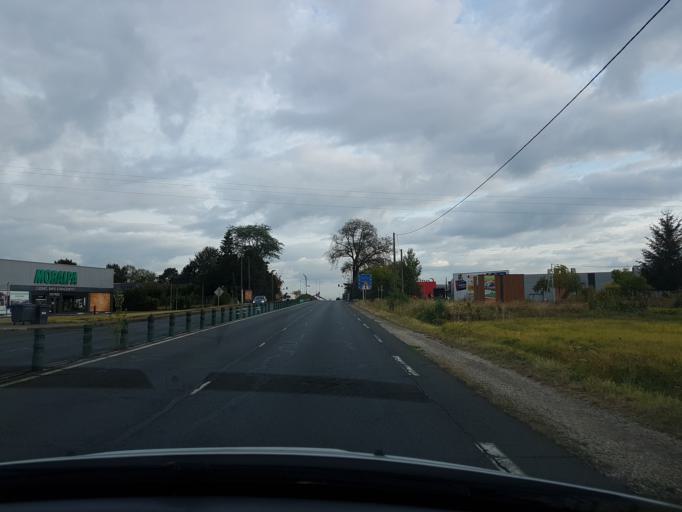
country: FR
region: Centre
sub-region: Departement d'Indre-et-Loire
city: Chambray-les-Tours
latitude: 47.3421
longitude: 0.7032
